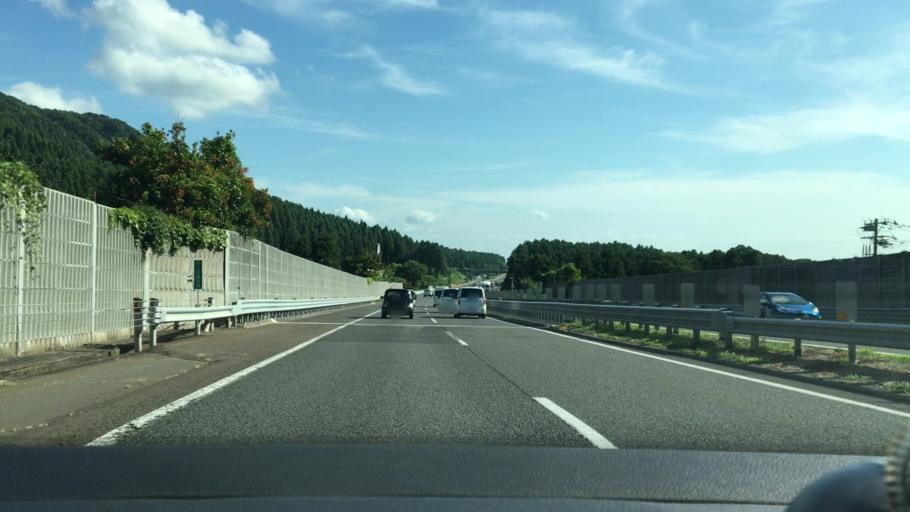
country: JP
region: Fukui
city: Maruoka
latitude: 36.1777
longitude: 136.2959
